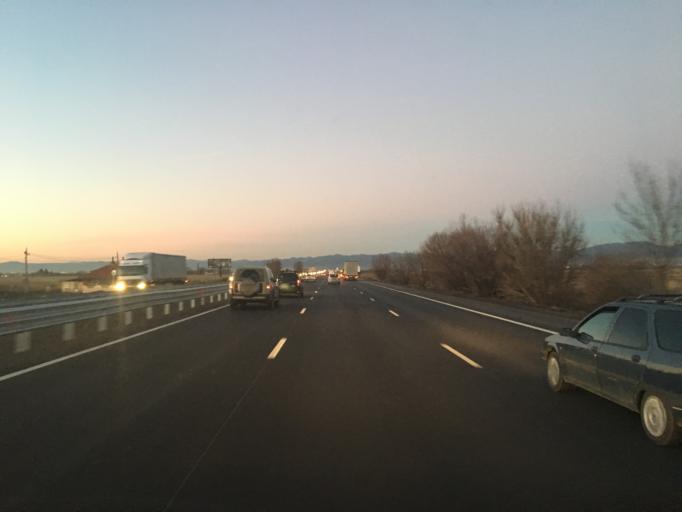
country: BG
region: Sofia-Capital
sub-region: Stolichna Obshtina
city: Sofia
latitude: 42.6878
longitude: 23.4533
